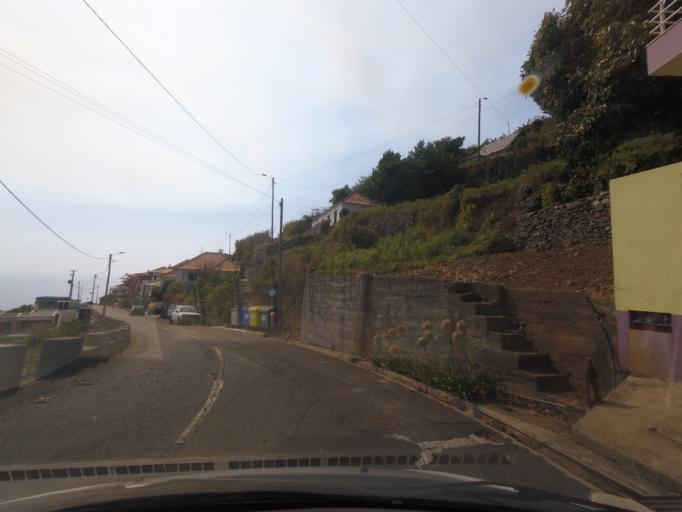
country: PT
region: Madeira
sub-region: Ribeira Brava
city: Campanario
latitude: 32.6876
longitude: -17.0649
